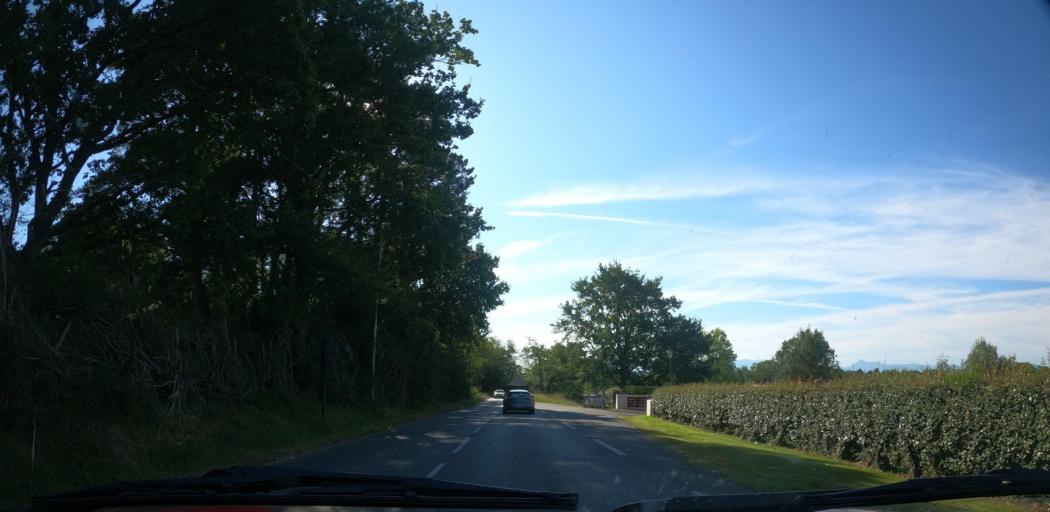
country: FR
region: Aquitaine
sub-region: Departement des Pyrenees-Atlantiques
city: Arbonne
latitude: 43.4055
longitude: -1.5380
